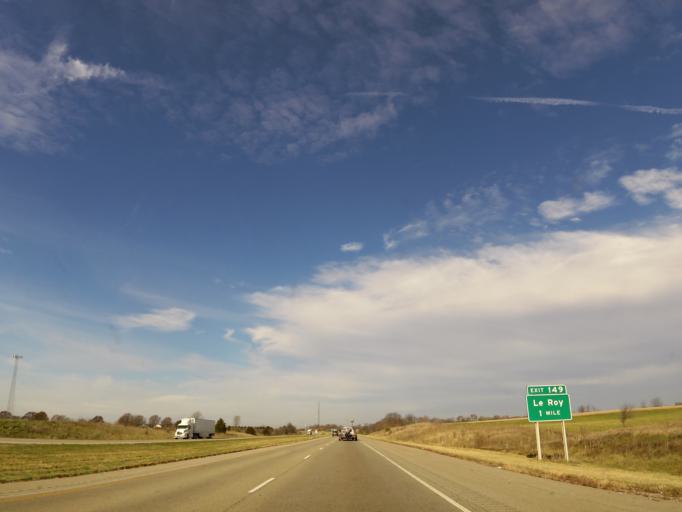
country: US
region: Illinois
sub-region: McLean County
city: Le Roy
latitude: 40.3281
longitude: -88.7460
